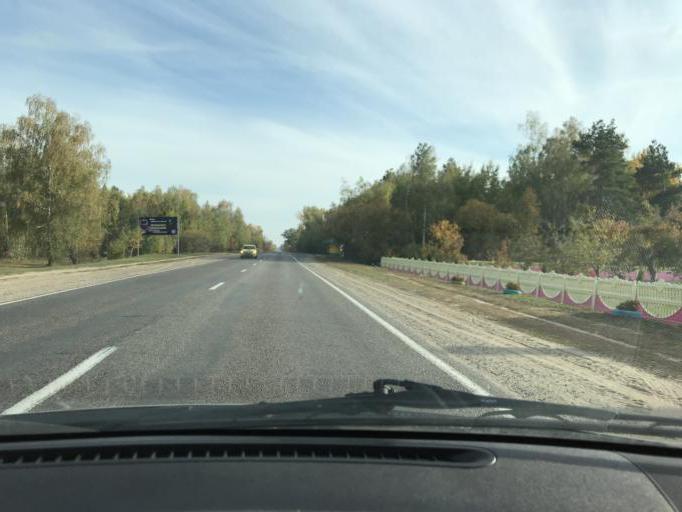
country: BY
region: Brest
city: Lahishyn
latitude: 52.2314
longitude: 26.0168
